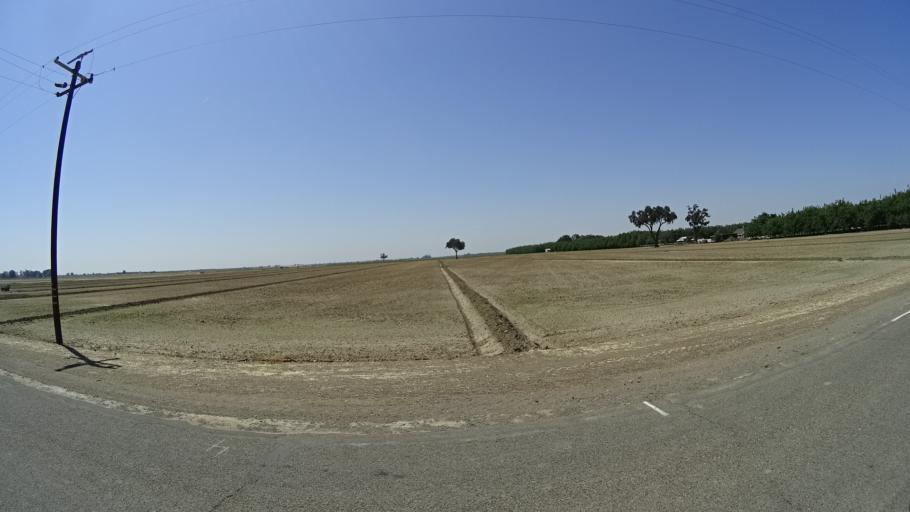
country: US
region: California
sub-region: Kings County
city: Lemoore
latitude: 36.3719
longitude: -119.7602
